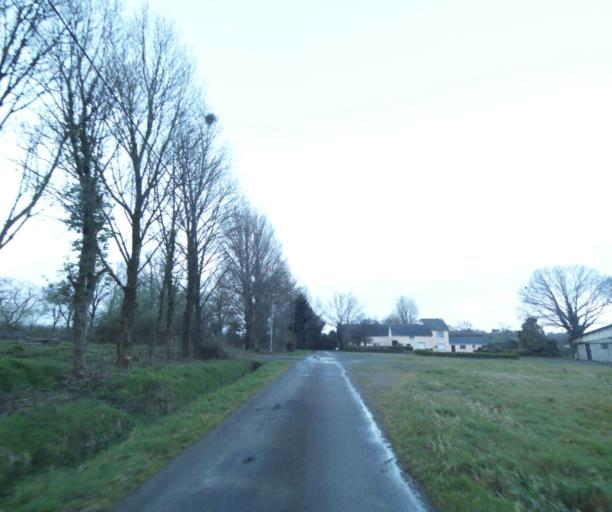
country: FR
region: Pays de la Loire
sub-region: Departement de la Loire-Atlantique
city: Malville
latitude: 47.3782
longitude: -1.8972
